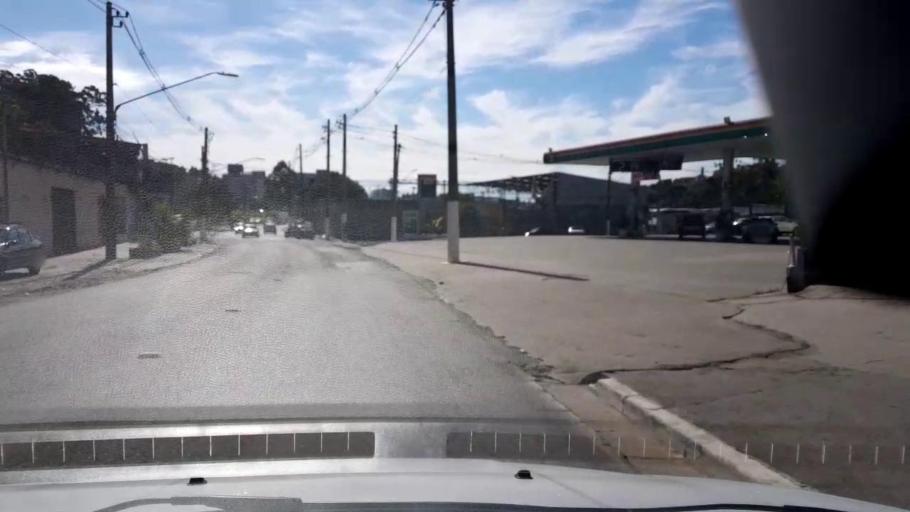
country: BR
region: Sao Paulo
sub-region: Ferraz De Vasconcelos
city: Ferraz de Vasconcelos
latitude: -23.5749
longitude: -46.4160
